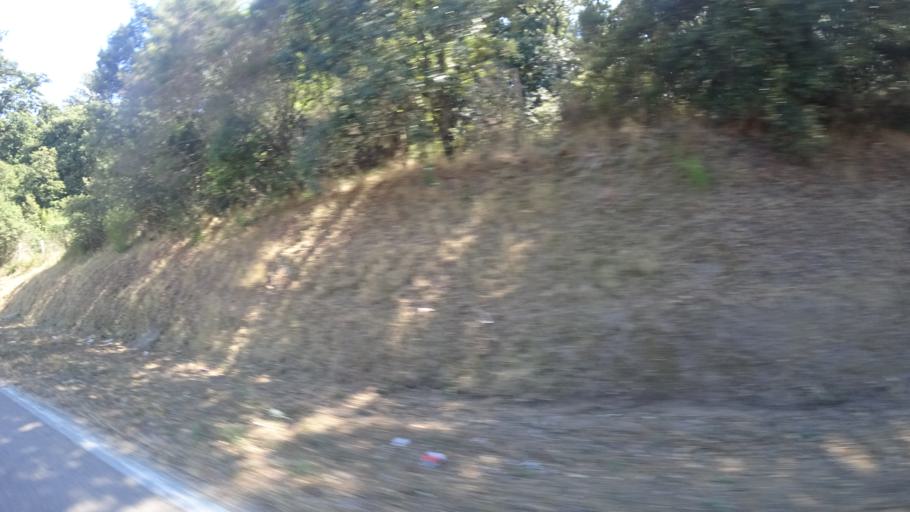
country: FR
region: Corsica
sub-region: Departement de la Corse-du-Sud
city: Alata
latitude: 41.9621
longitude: 8.7258
